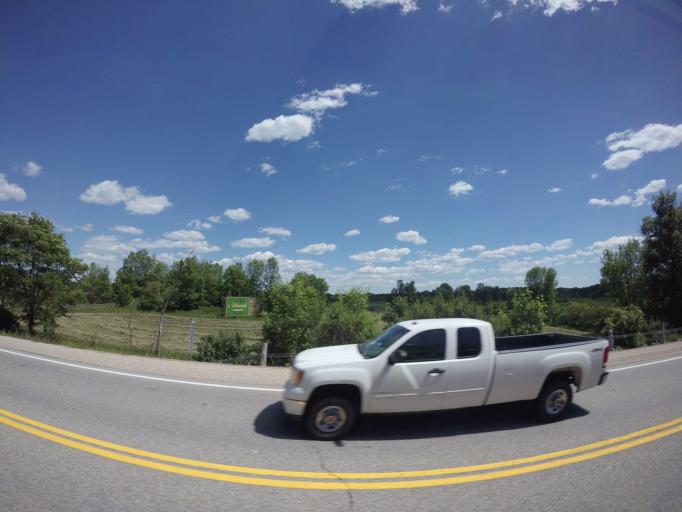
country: CA
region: Ontario
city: Carleton Place
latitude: 45.1237
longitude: -76.2103
